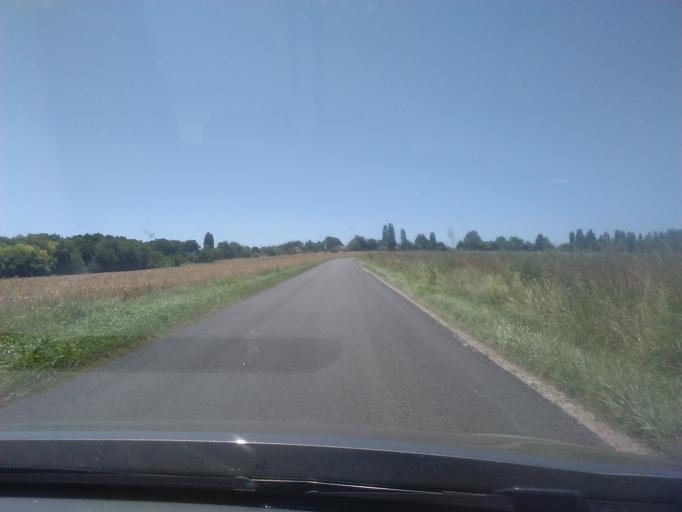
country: FR
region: Centre
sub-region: Departement du Loir-et-Cher
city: Saint-Sulpice-de-Pommeray
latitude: 47.6019
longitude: 1.2210
